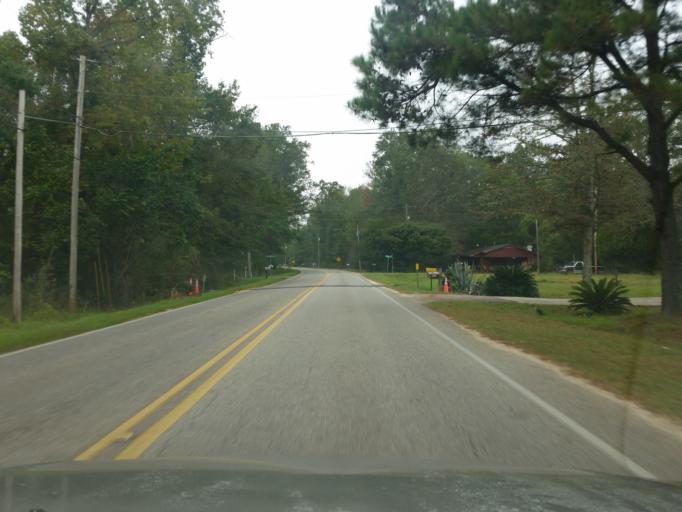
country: US
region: Alabama
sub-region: Baldwin County
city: Bay Minette
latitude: 30.8645
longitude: -87.7945
